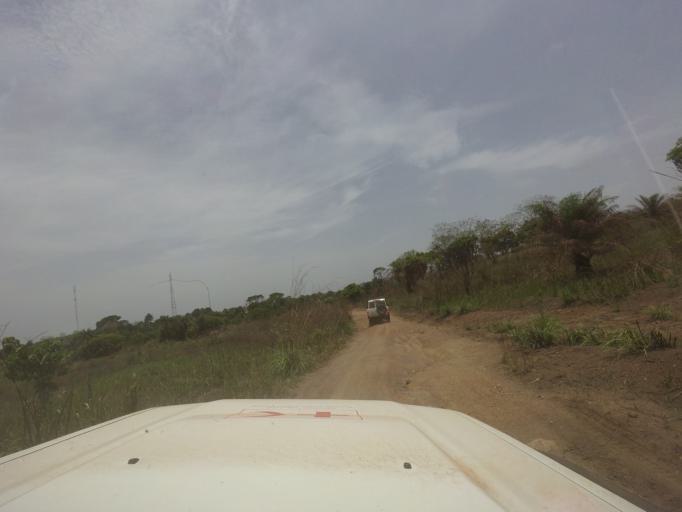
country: GN
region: Nzerekore
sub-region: Prefecture de Guekedou
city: Gueckedou
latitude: 8.4986
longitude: -10.3323
